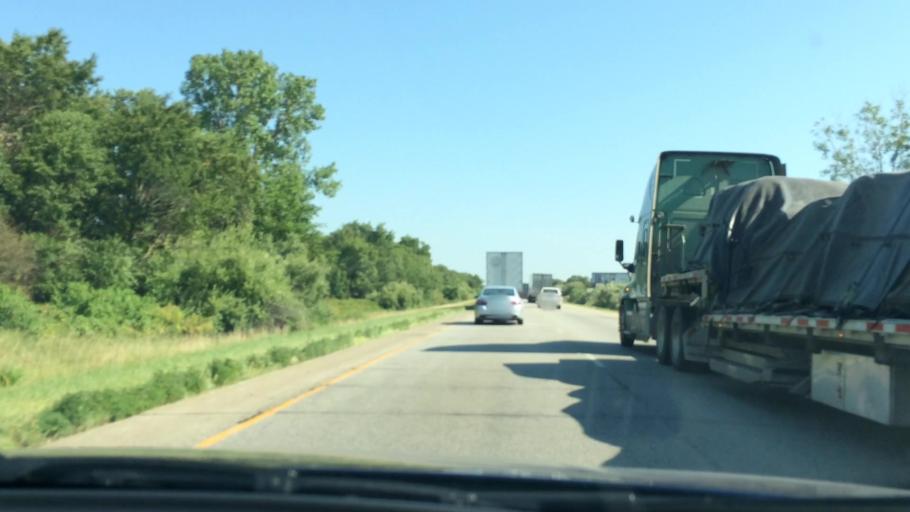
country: US
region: Indiana
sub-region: Newton County
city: Roselawn
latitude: 41.0267
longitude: -87.2703
